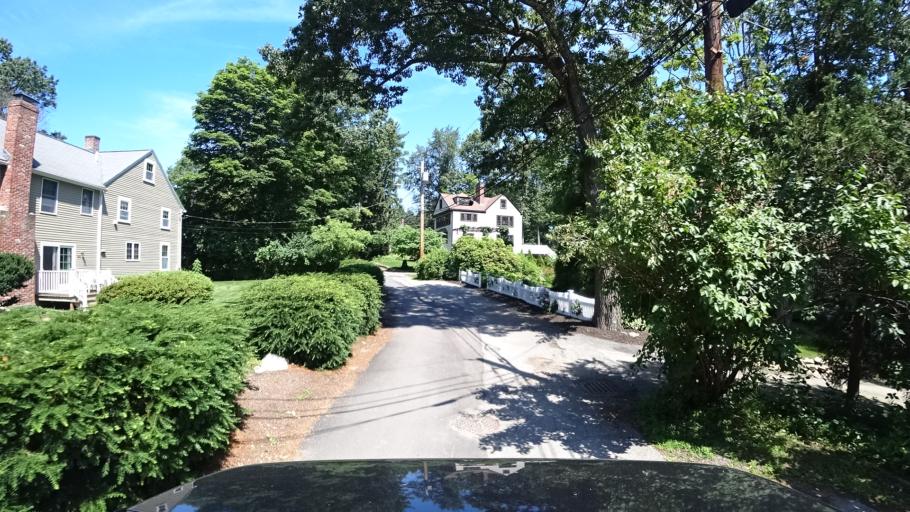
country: US
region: Massachusetts
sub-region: Norfolk County
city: Dedham
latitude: 42.2433
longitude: -71.1594
